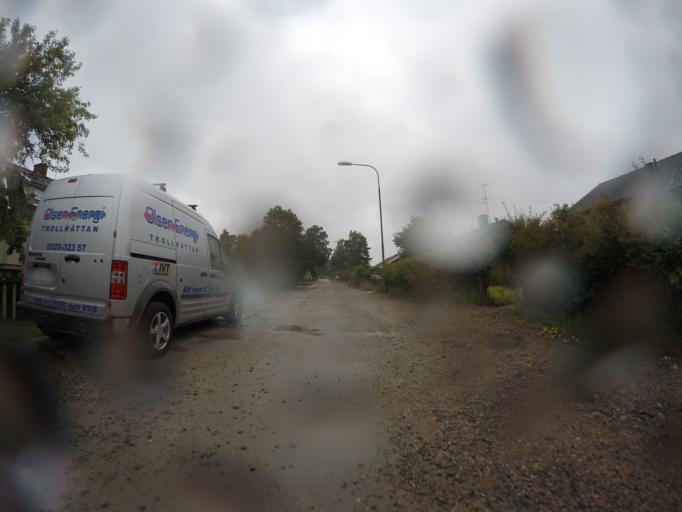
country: SE
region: Vaestra Goetaland
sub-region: Trollhattan
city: Sjuntorp
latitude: 58.1607
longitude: 12.3034
